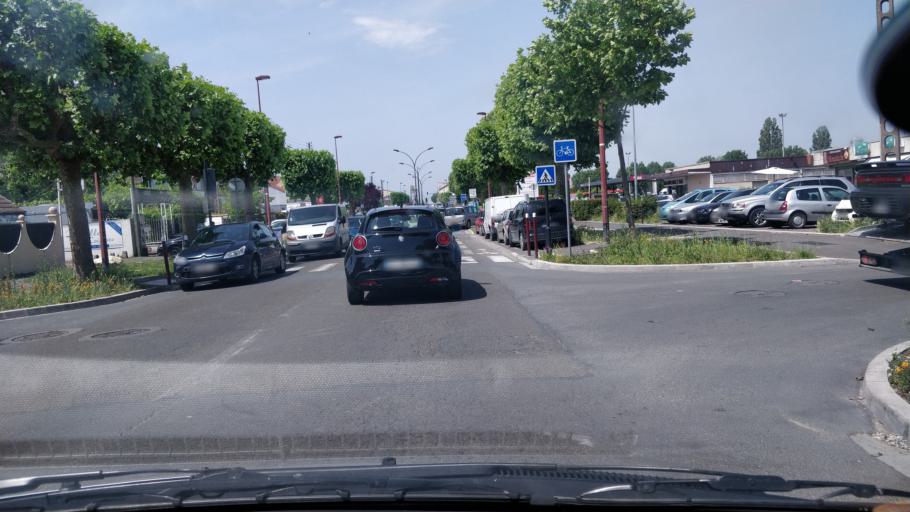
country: FR
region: Ile-de-France
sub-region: Departement de Seine-Saint-Denis
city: Clichy-sous-Bois
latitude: 48.8986
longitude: 2.5506
